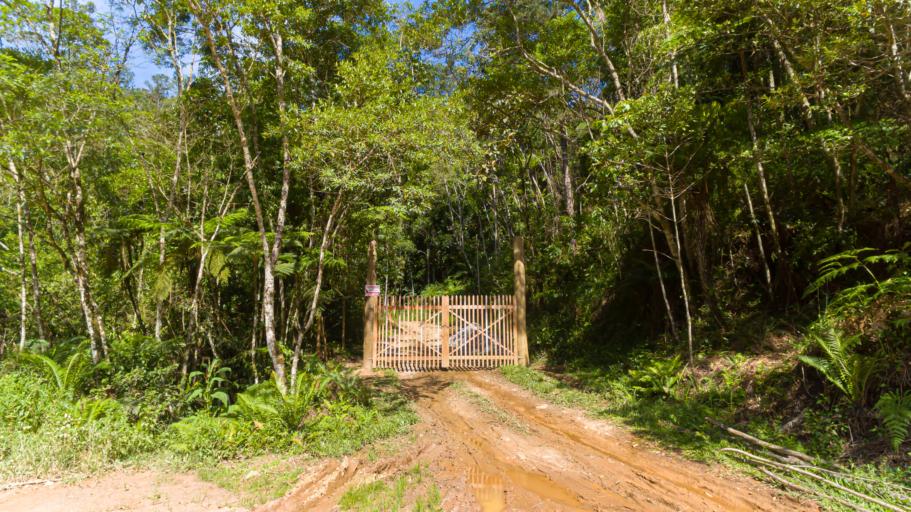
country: BR
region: Sao Paulo
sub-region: Juquitiba
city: Juquitiba
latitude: -24.0387
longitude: -47.2483
